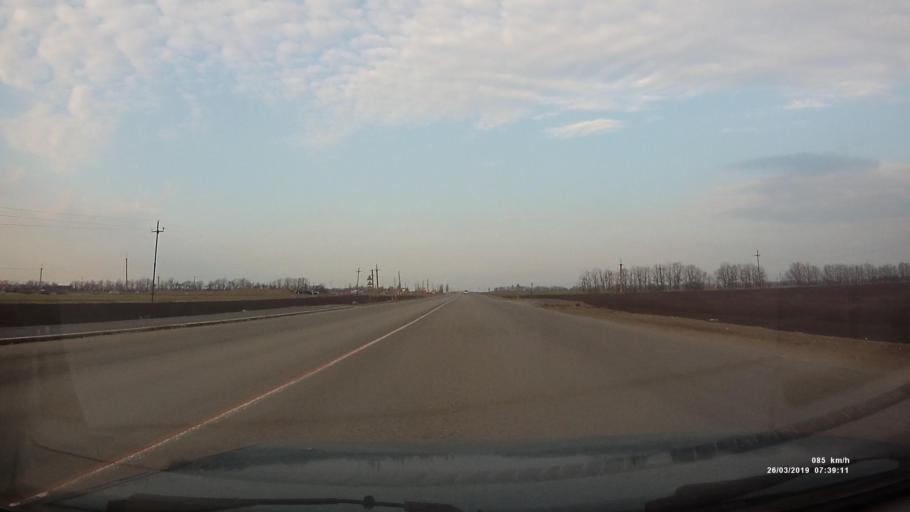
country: RU
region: Rostov
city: Novobessergenovka
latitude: 47.1976
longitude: 38.6699
